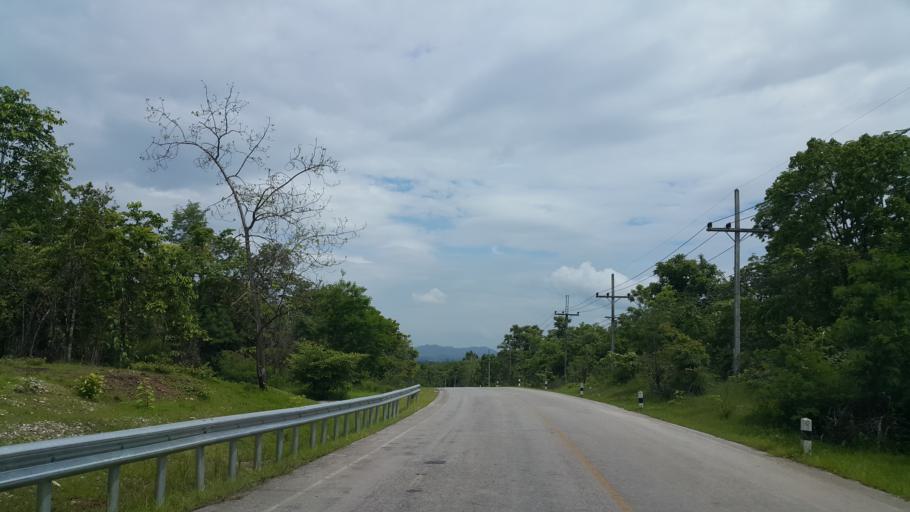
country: TH
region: Lampang
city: Mueang Pan
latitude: 18.7731
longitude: 99.5521
